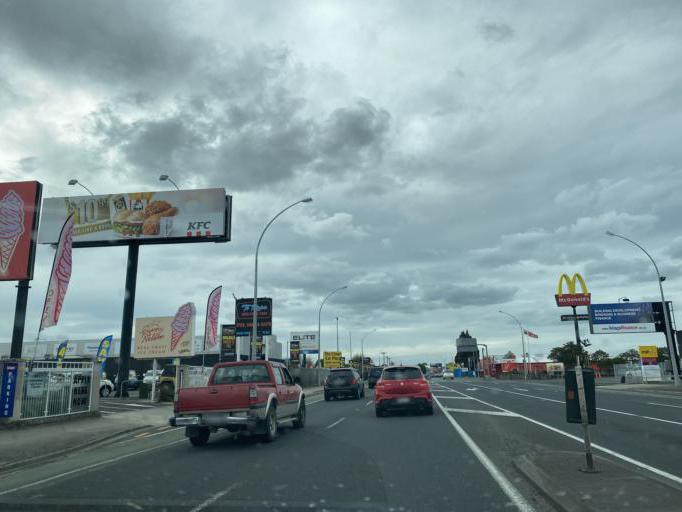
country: NZ
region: Waikato
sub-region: Hamilton City
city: Hamilton
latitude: -37.7947
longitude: 175.2606
